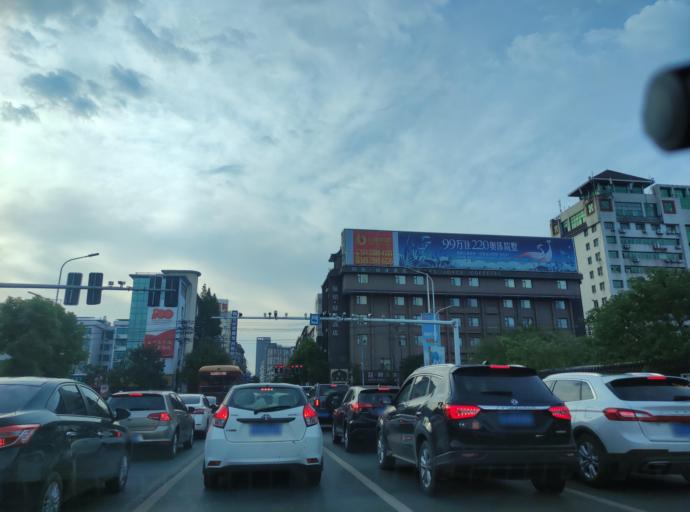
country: CN
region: Jiangxi Sheng
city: Pingxiang
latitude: 27.6347
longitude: 113.8575
